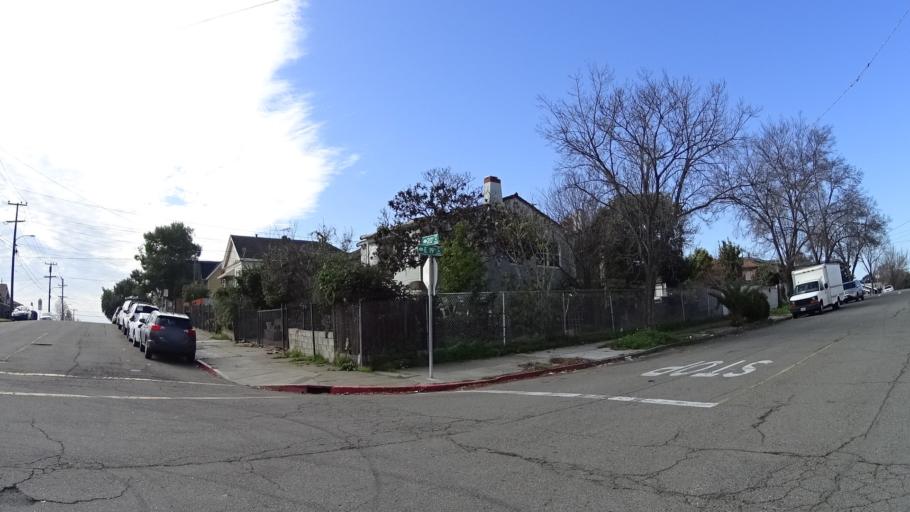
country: US
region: California
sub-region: Alameda County
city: Alameda
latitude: 37.7892
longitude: -122.2369
